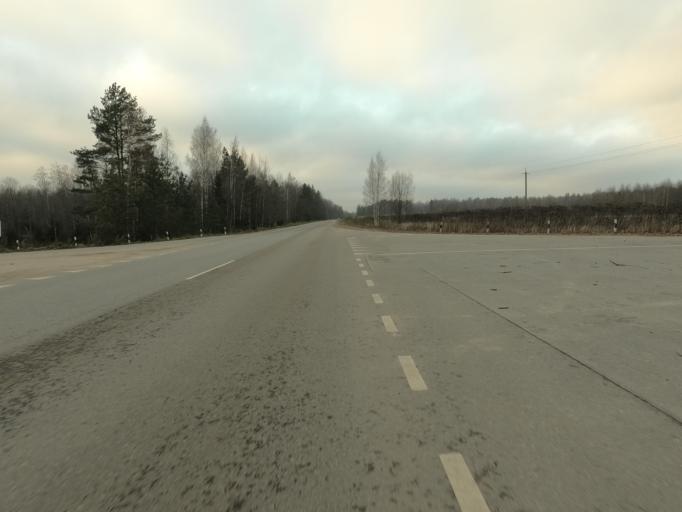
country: RU
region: Leningrad
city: Kirovsk
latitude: 59.8024
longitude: 30.9825
